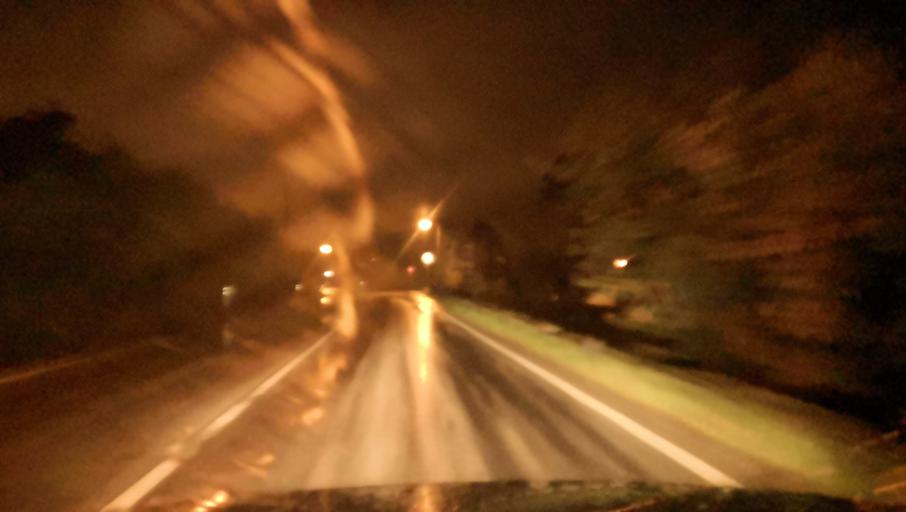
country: PT
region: Vila Real
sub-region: Vila Real
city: Vila Real
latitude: 41.3340
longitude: -7.7290
